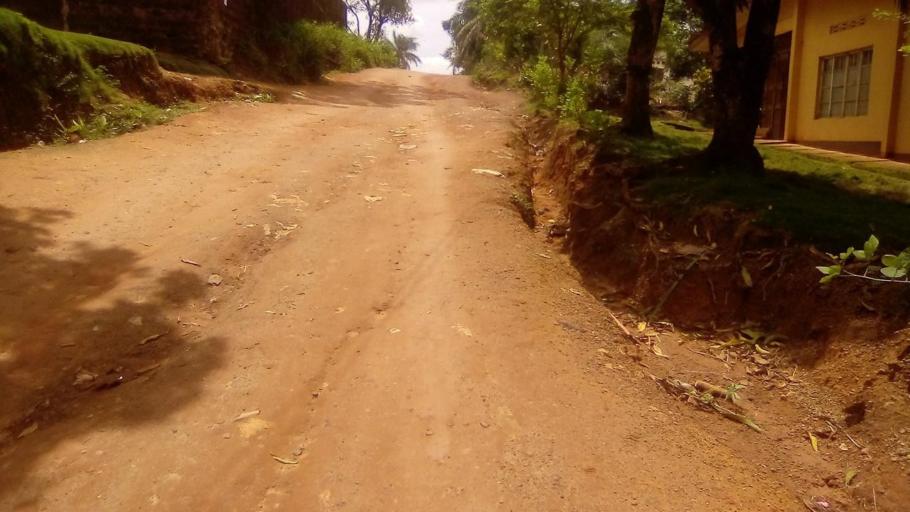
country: SL
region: Southern Province
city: Bo
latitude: 7.9438
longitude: -11.7354
